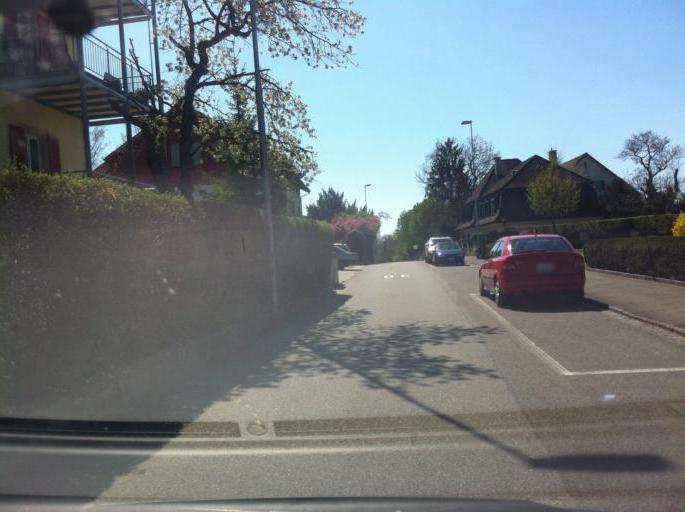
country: CH
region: Schaffhausen
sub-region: Bezirk Schaffhausen
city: Schaffhausen
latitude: 47.7079
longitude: 8.6324
